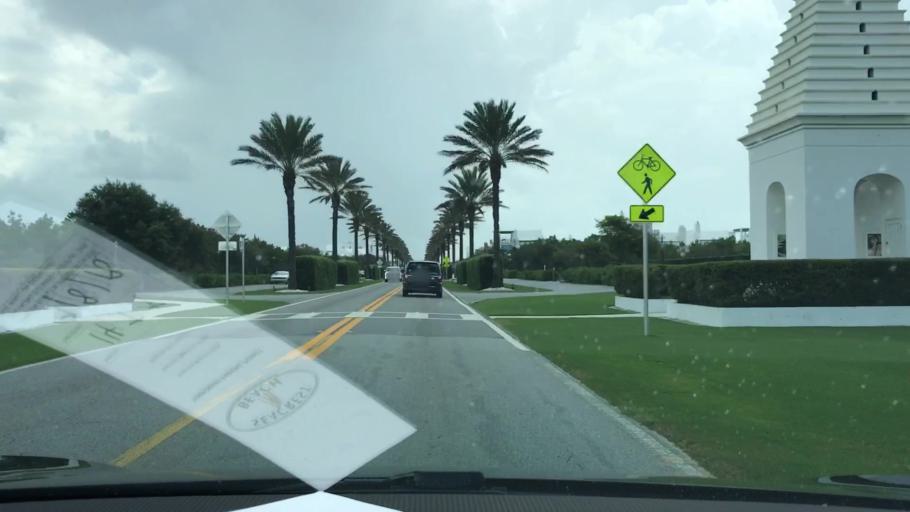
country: US
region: Florida
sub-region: Walton County
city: Seaside
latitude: 30.2863
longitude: -86.0331
